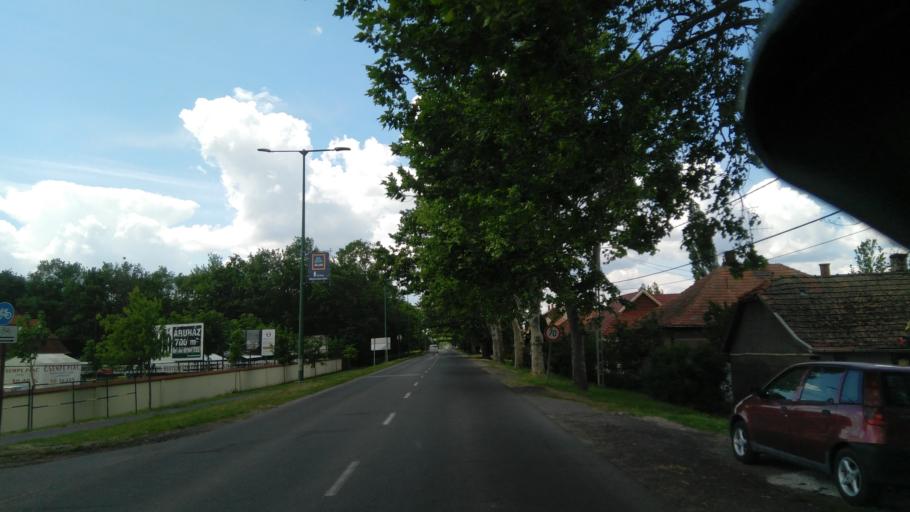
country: HU
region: Bekes
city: Gyula
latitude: 46.6451
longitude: 21.2554
